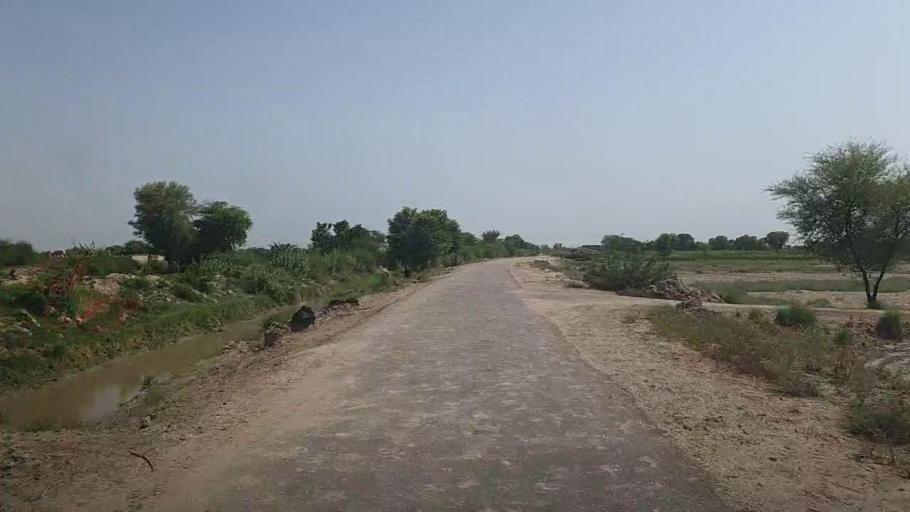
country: PK
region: Sindh
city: Pad Idan
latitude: 26.8303
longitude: 68.3305
